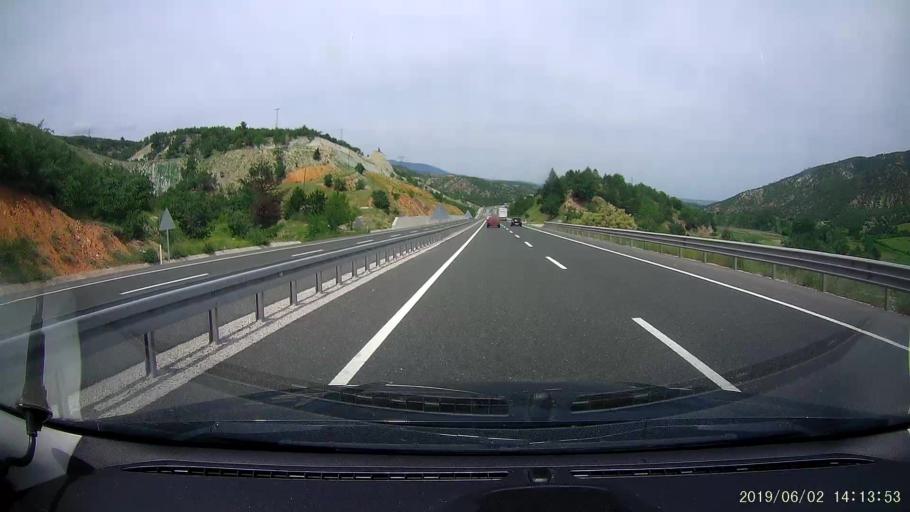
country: TR
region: Cankiri
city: Yaprakli
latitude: 40.9292
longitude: 33.8415
